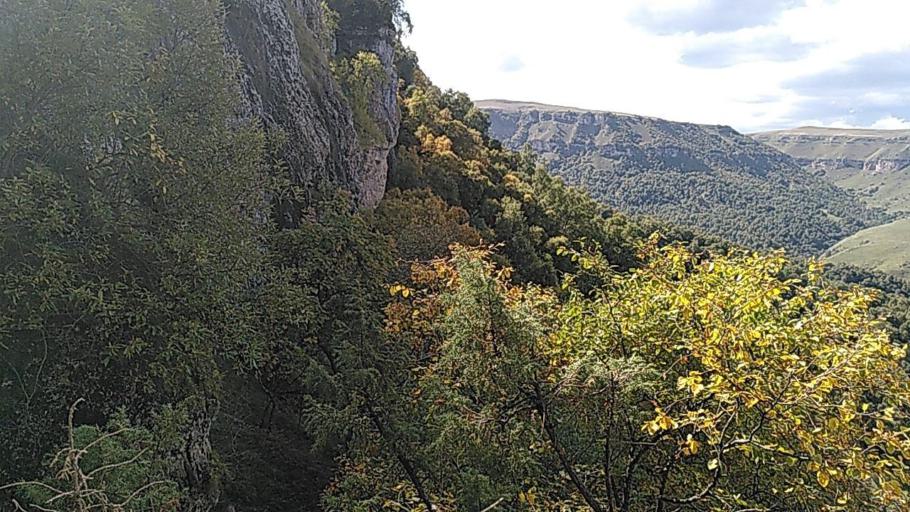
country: RU
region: Kabardino-Balkariya
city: Kamennomostskoye
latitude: 43.6716
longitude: 42.8172
